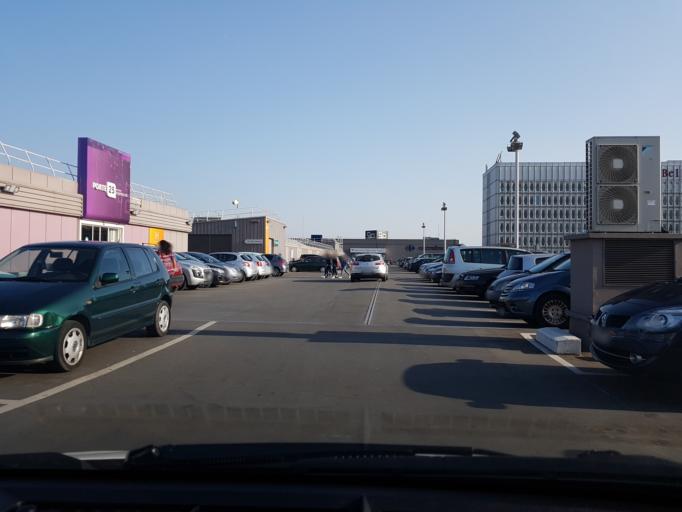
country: FR
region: Ile-de-France
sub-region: Departement du Val-de-Marne
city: Rungis
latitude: 48.7568
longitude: 2.3707
